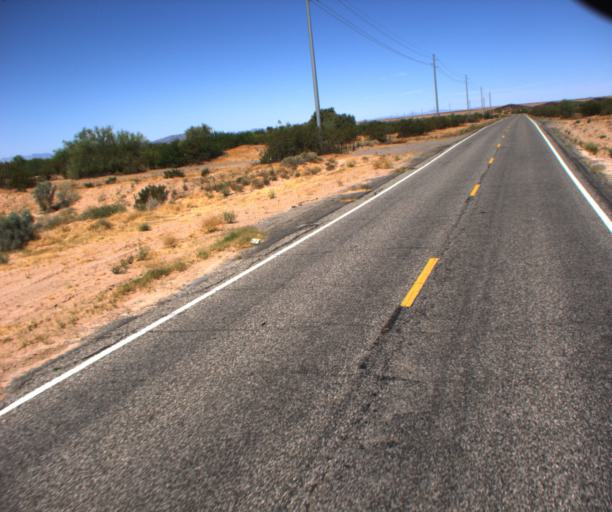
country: US
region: Arizona
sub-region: La Paz County
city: Cienega Springs
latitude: 33.9884
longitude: -114.0743
